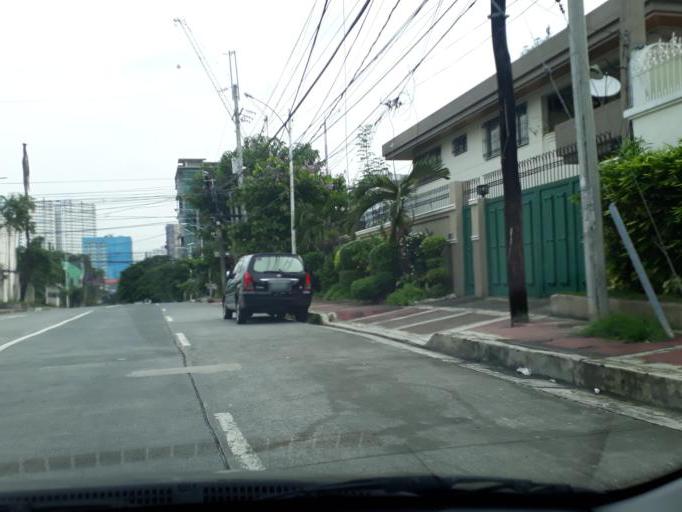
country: PH
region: Calabarzon
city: Del Monte
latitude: 14.6328
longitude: 121.0327
